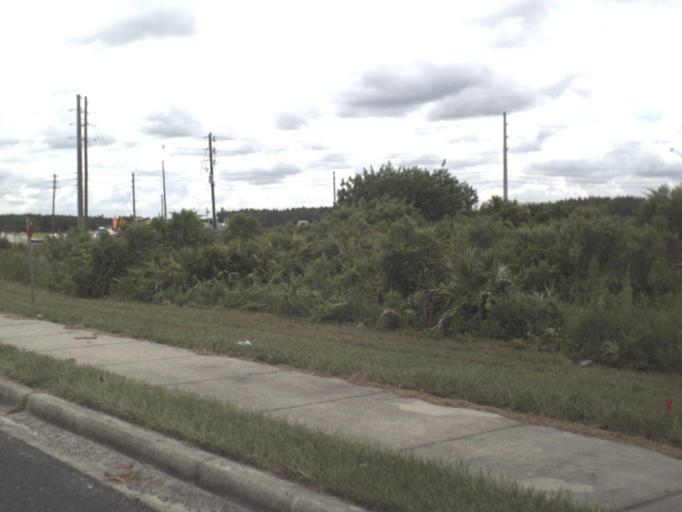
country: US
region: Florida
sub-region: Pasco County
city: Odessa
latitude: 28.1905
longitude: -82.6152
